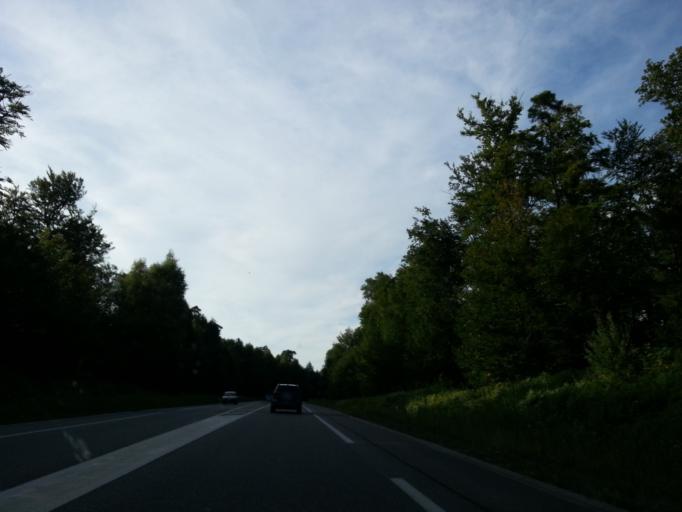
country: FR
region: Alsace
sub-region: Departement du Bas-Rhin
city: Walbourg
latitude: 48.8757
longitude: 7.8262
